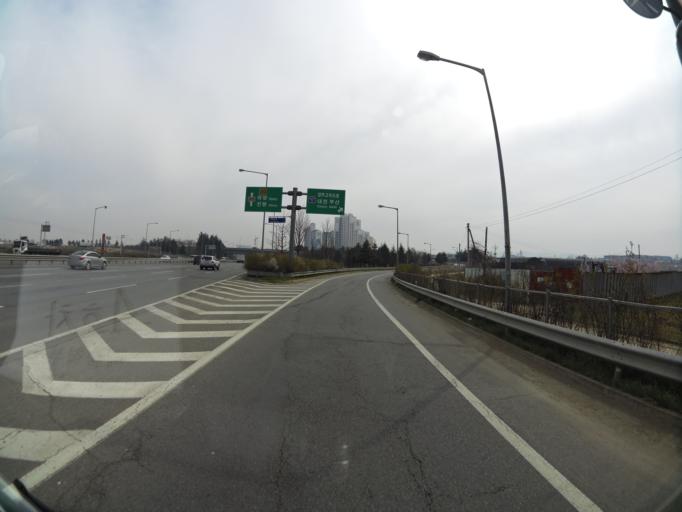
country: KR
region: Gyeongsangbuk-do
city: Hayang
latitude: 35.8739
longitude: 128.7939
